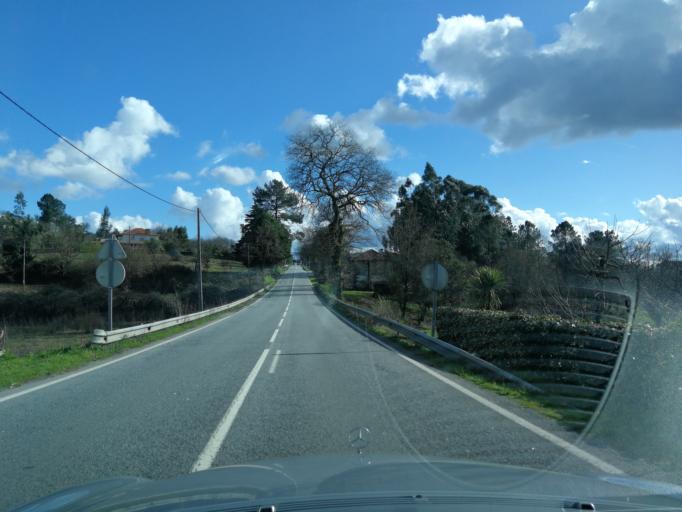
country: PT
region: Braga
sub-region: Vila Verde
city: Prado
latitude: 41.6731
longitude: -8.5238
